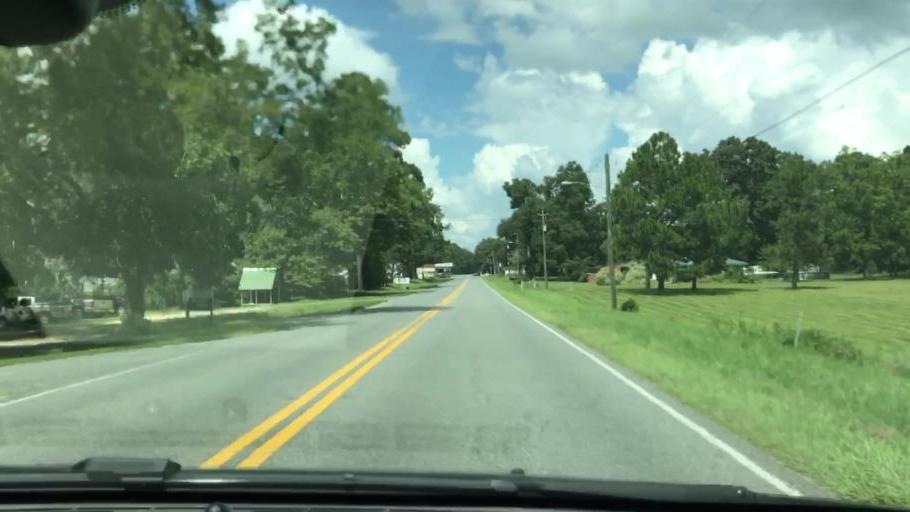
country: US
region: Florida
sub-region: Jackson County
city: Malone
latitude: 30.9234
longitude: -85.1186
